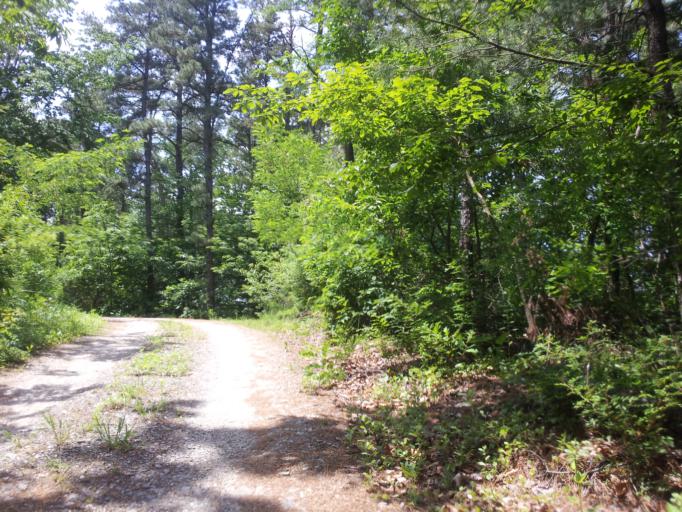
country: KR
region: Daejeon
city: Sintansin
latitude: 36.4408
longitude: 127.4882
